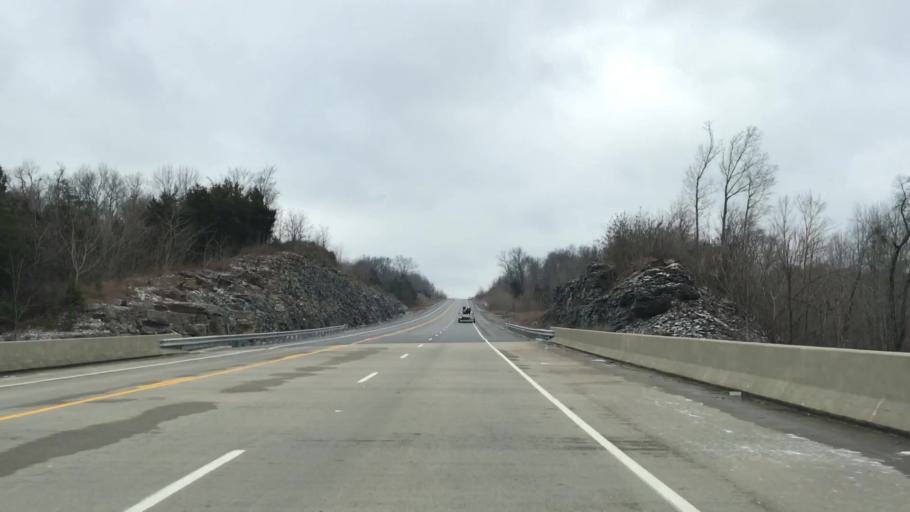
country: US
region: Kentucky
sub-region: Adair County
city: Columbia
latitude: 37.0319
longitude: -85.3811
